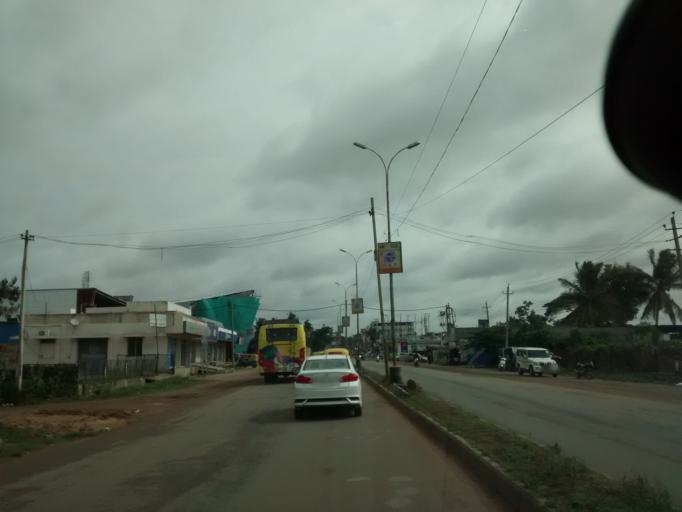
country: IN
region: Karnataka
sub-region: Tumkur
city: Tumkur
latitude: 13.3565
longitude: 77.1033
